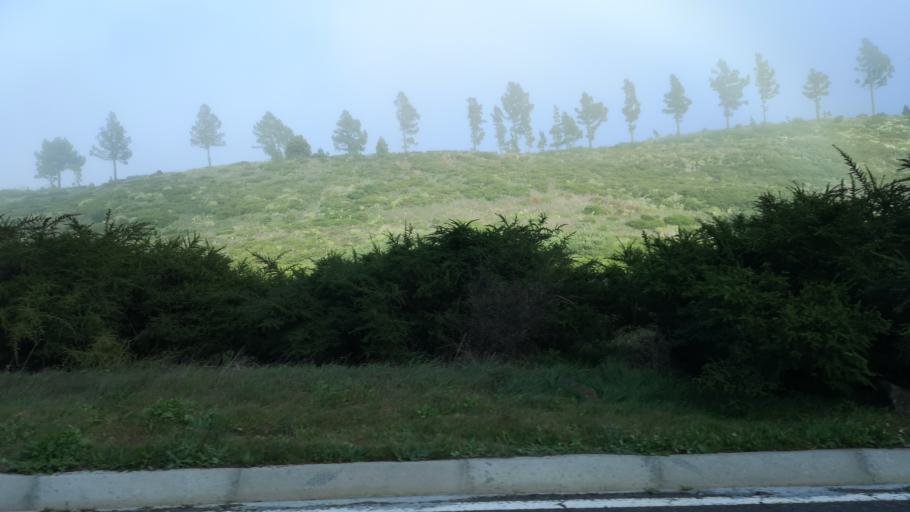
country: ES
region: Canary Islands
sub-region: Provincia de Santa Cruz de Tenerife
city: Alajero
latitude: 28.0971
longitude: -17.2480
